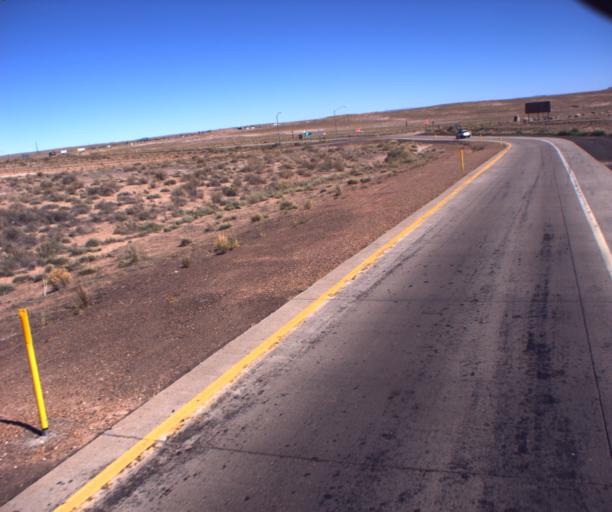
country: US
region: Arizona
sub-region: Navajo County
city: Holbrook
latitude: 34.9719
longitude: -110.0879
